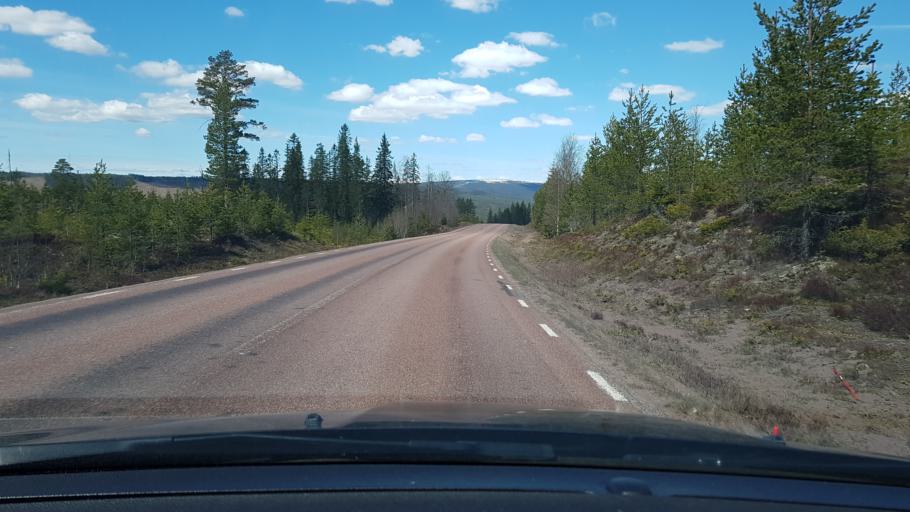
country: SE
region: Dalarna
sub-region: Malung-Saelens kommun
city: Malung
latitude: 61.0489
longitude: 13.3705
